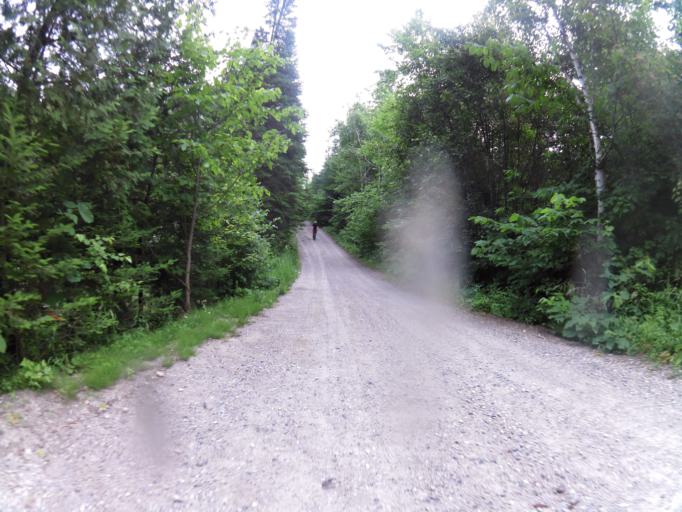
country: CA
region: Ontario
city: Perth
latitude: 45.0097
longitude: -76.5914
